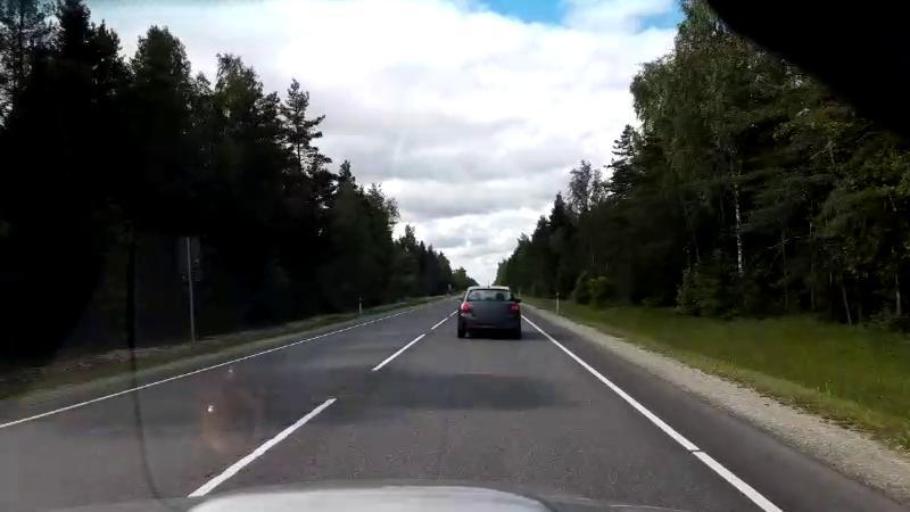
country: EE
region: Raplamaa
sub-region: Maerjamaa vald
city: Marjamaa
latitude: 58.8821
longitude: 24.4494
